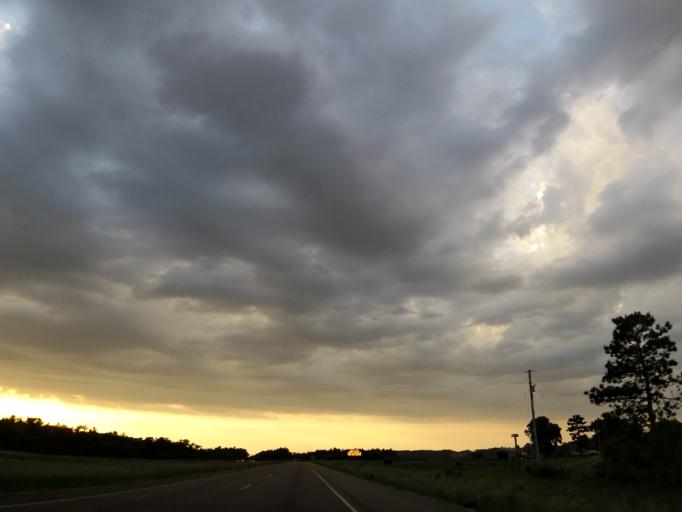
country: US
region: Wisconsin
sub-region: Eau Claire County
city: Altoona
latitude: 44.7419
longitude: -91.3762
